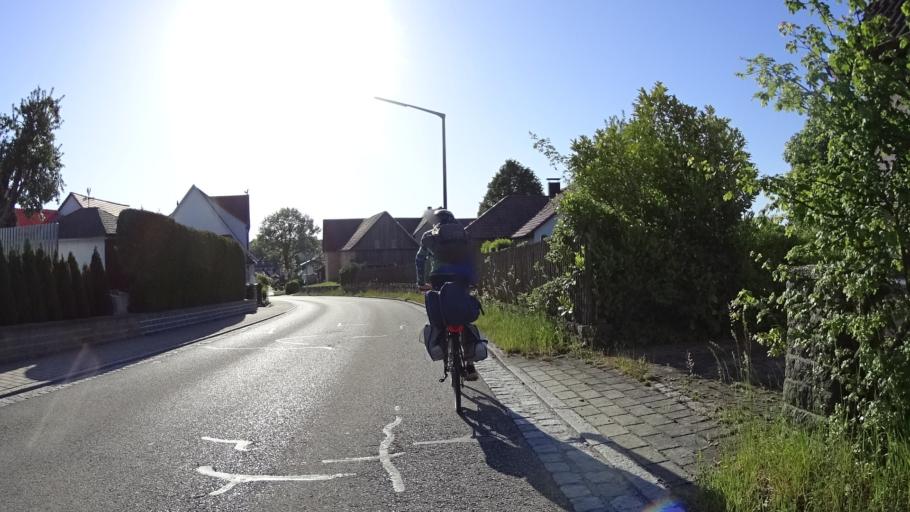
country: DE
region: Bavaria
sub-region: Regierungsbezirk Mittelfranken
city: Dentlein am Forst
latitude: 49.1481
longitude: 10.4189
